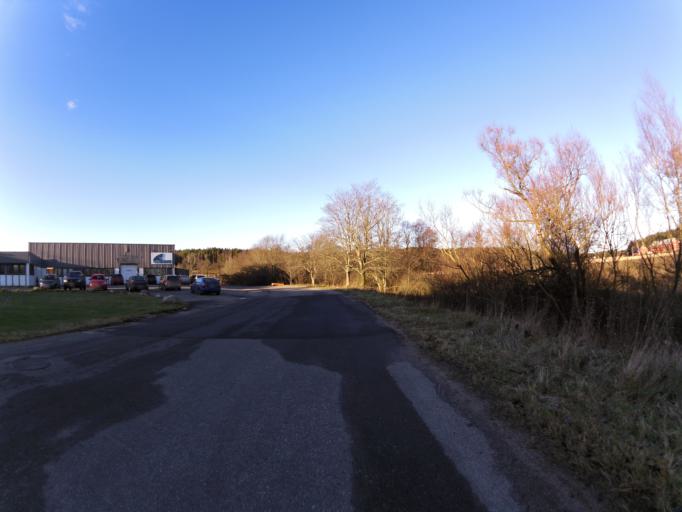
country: NO
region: Ostfold
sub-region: Fredrikstad
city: Fredrikstad
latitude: 59.2451
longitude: 10.9774
